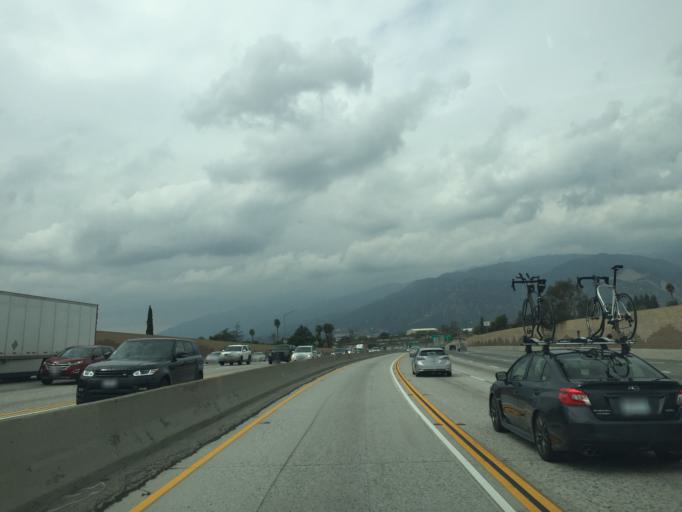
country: US
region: California
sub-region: Los Angeles County
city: Azusa
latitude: 34.1220
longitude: -117.9116
